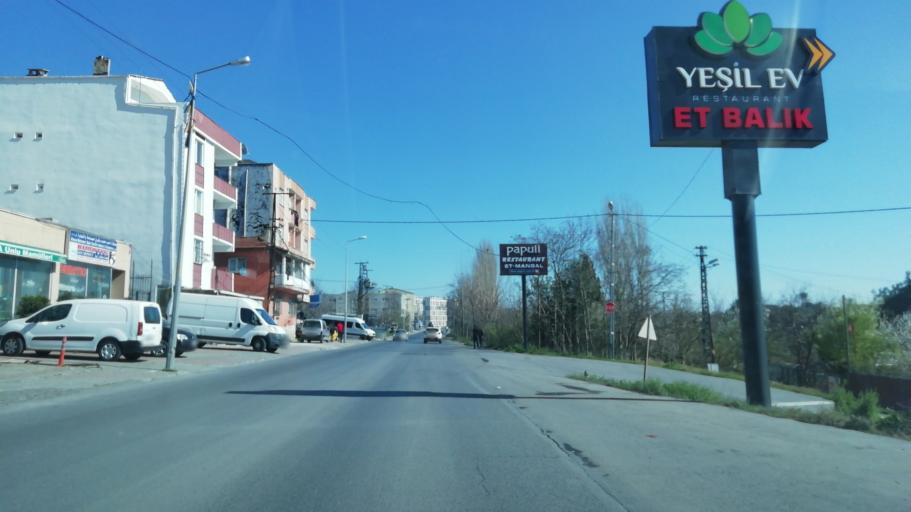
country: TR
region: Istanbul
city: Basaksehir
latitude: 41.0439
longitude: 28.7530
